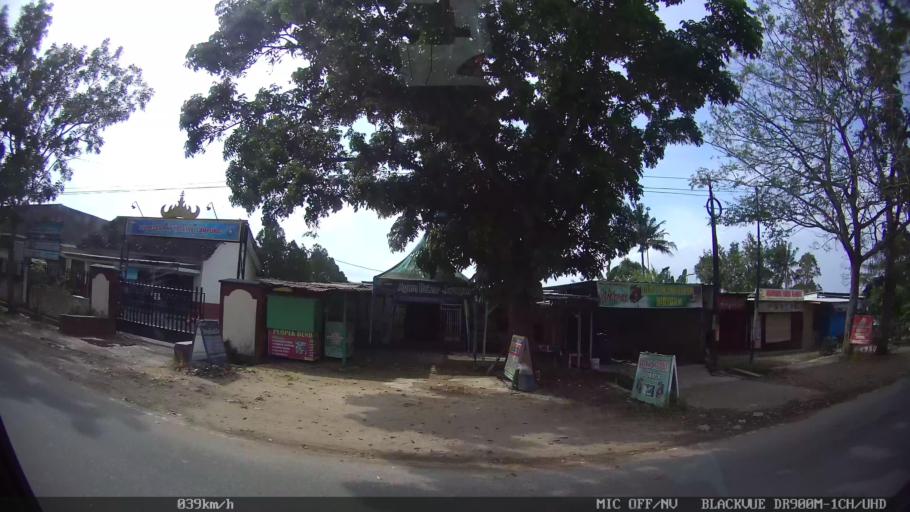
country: ID
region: Lampung
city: Kedaton
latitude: -5.3809
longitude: 105.3001
